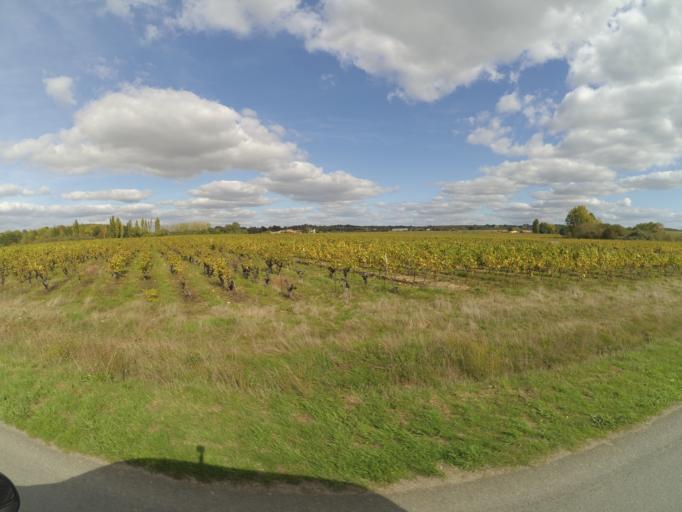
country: FR
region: Pays de la Loire
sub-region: Departement de la Loire-Atlantique
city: Le Loroux-Bottereau
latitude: 47.2088
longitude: -1.3506
